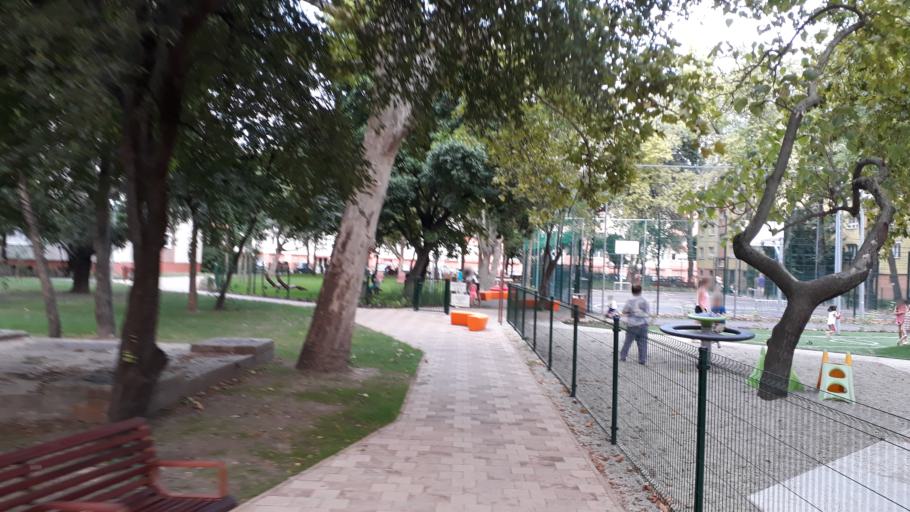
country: HU
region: Budapest
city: Budapest XI. keruelet
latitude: 47.4547
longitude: 19.0308
